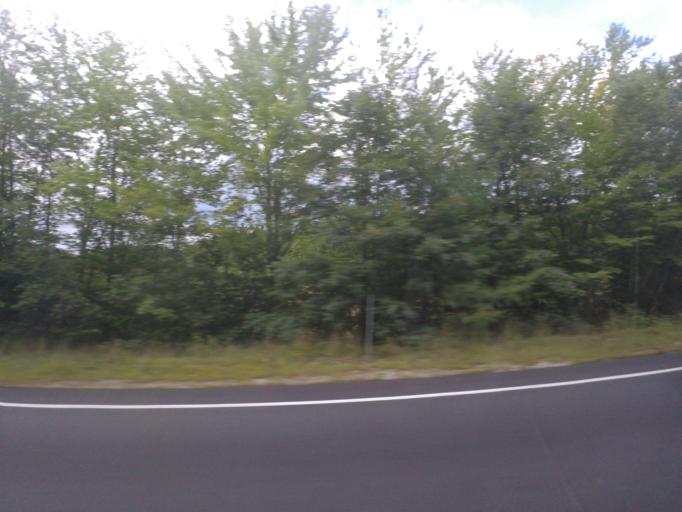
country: US
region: New Hampshire
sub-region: Rockingham County
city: Northwood
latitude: 43.2020
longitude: -71.1070
